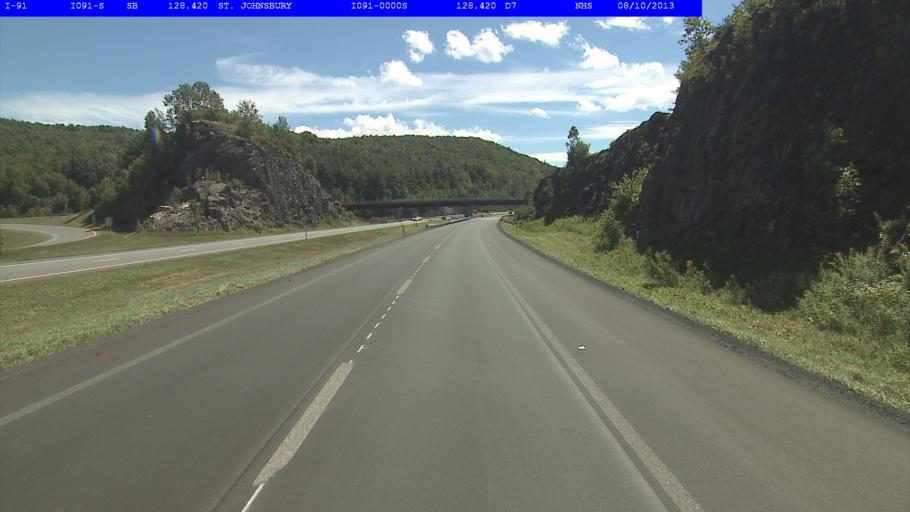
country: US
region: Vermont
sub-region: Caledonia County
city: Saint Johnsbury
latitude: 44.3987
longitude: -72.0189
